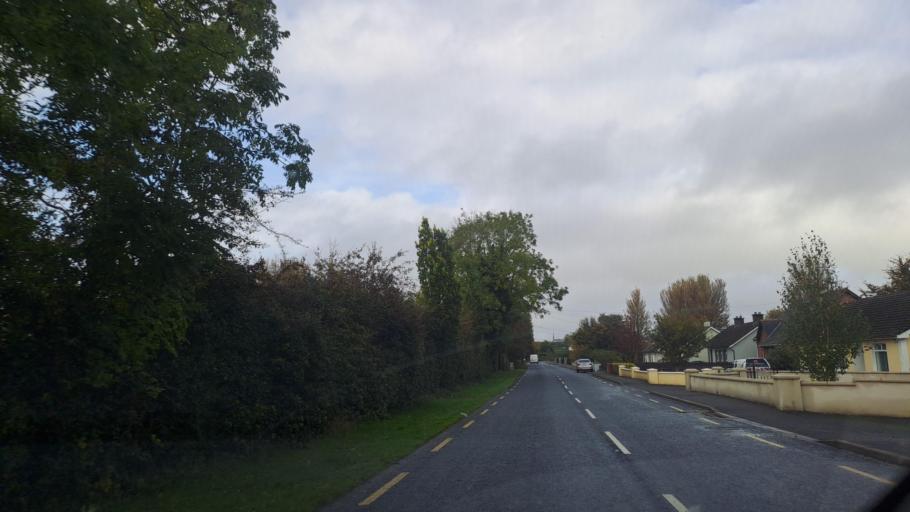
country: IE
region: Ulster
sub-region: County Monaghan
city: Carrickmacross
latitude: 53.9588
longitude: -6.7120
